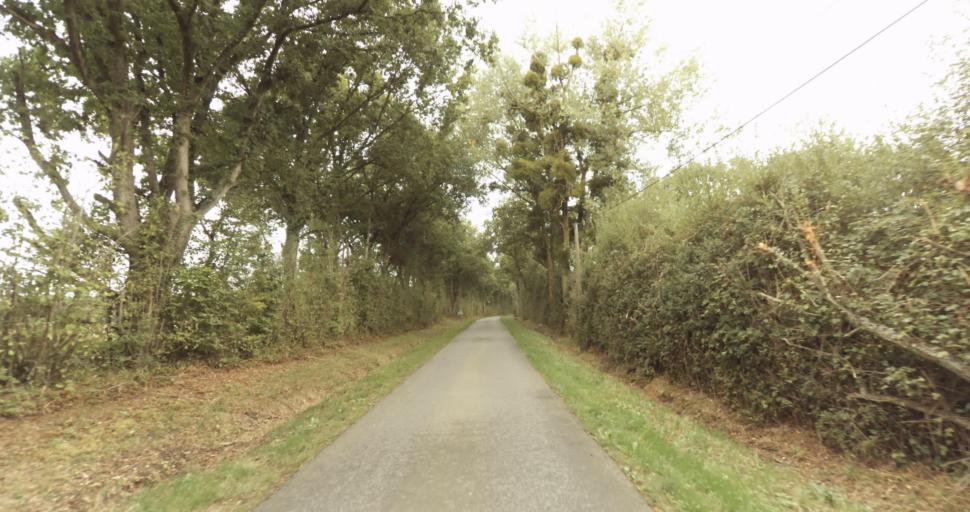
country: FR
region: Lower Normandy
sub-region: Departement de l'Orne
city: Sees
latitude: 48.6800
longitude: 0.2622
